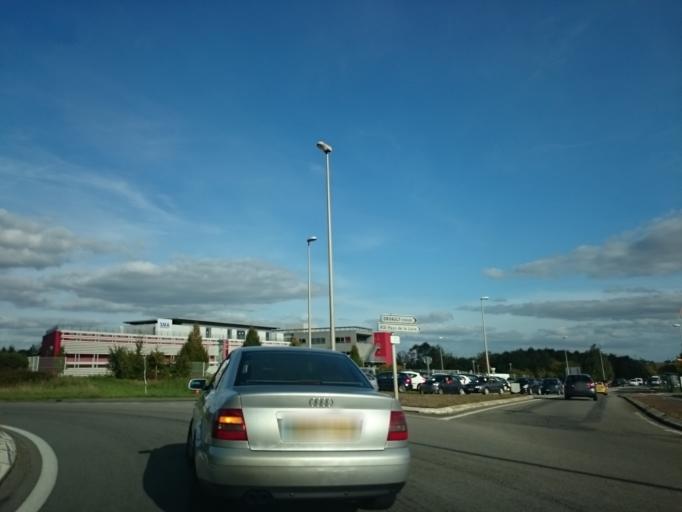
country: FR
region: Pays de la Loire
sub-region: Departement de la Loire-Atlantique
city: Orvault
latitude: 47.2581
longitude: -1.6241
